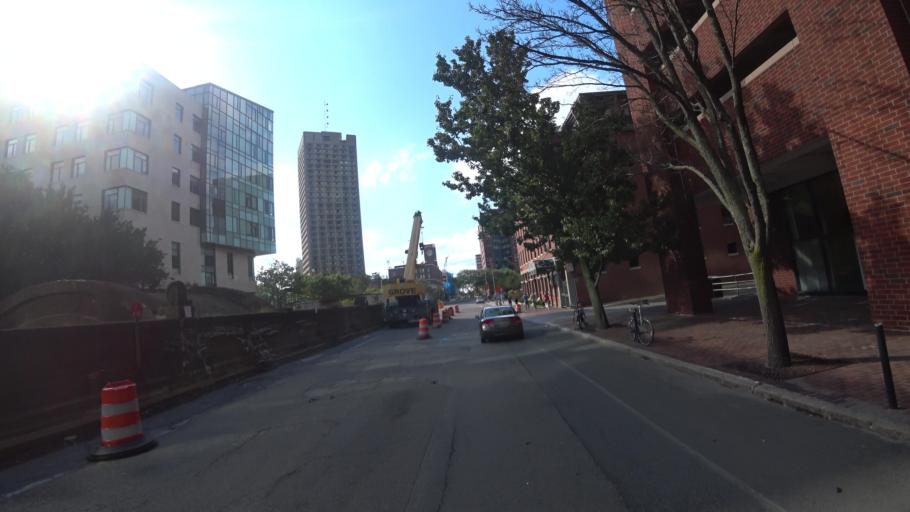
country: US
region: Massachusetts
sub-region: Suffolk County
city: Boston
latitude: 42.3621
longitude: -71.0817
